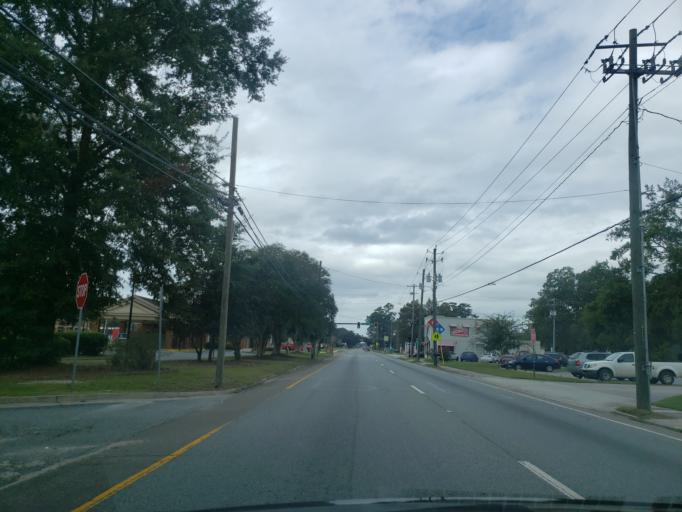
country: US
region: Georgia
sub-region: Chatham County
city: Pooler
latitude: 32.1157
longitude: -81.2475
